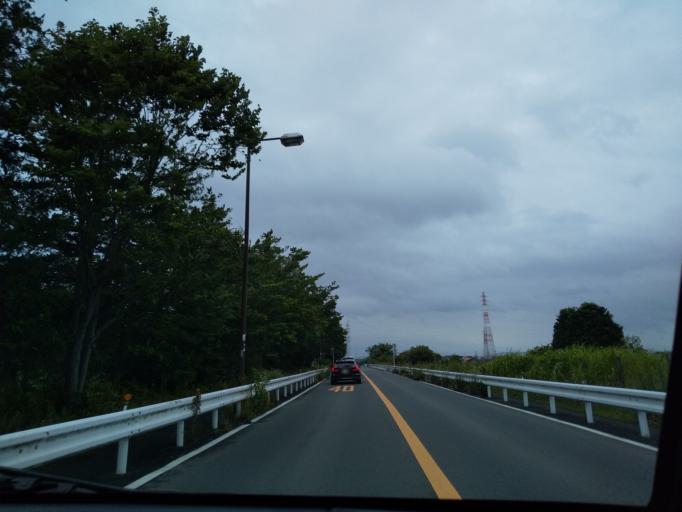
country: JP
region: Kanagawa
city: Fujisawa
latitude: 35.3987
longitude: 139.5035
